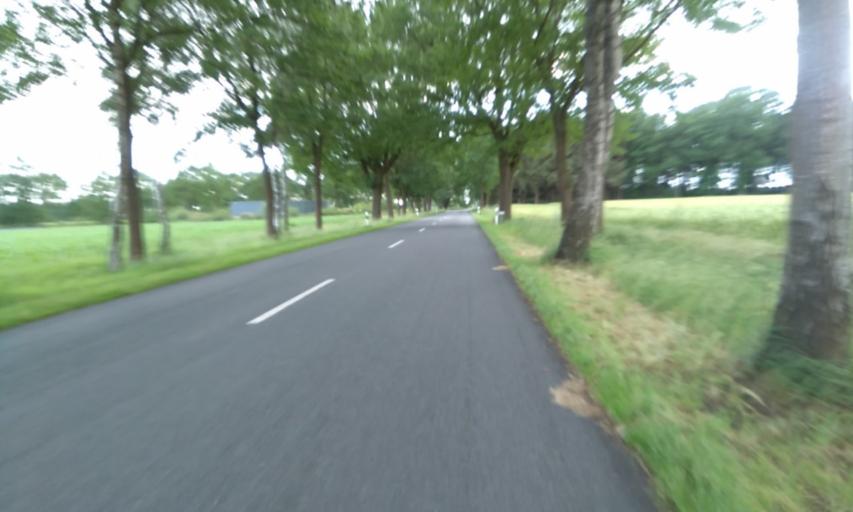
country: DE
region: Lower Saxony
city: Wohnste
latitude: 53.3586
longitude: 9.5556
